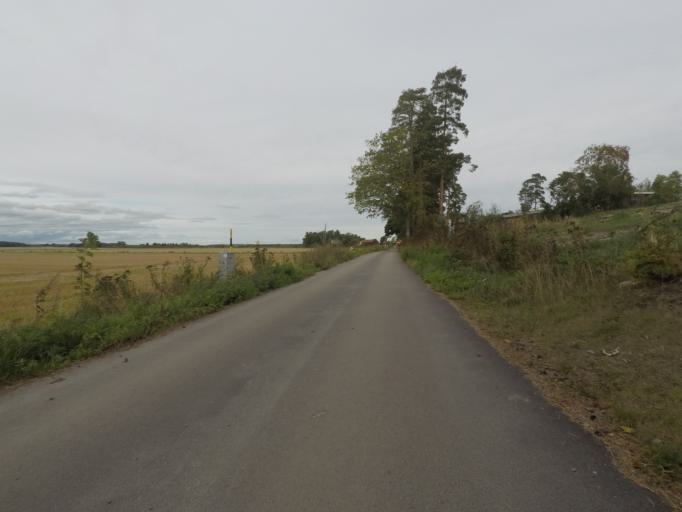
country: SE
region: Vaestmanland
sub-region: Kungsors Kommun
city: Kungsoer
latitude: 59.4534
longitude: 16.0751
